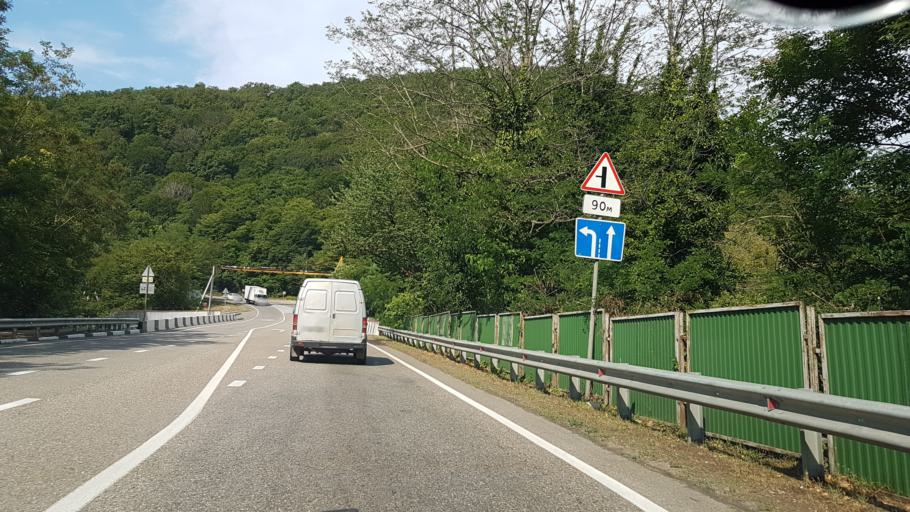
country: RU
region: Krasnodarskiy
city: Nebug
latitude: 44.1773
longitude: 38.9755
